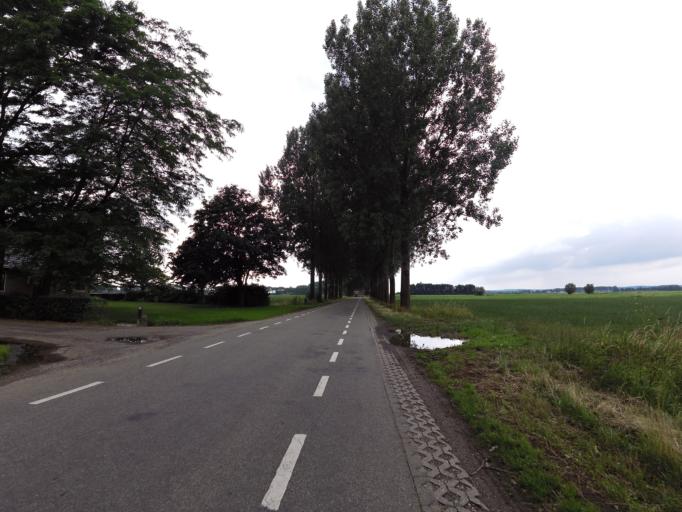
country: NL
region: Gelderland
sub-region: Gemeente Zevenaar
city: Zevenaar
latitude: 51.9689
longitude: 6.1069
